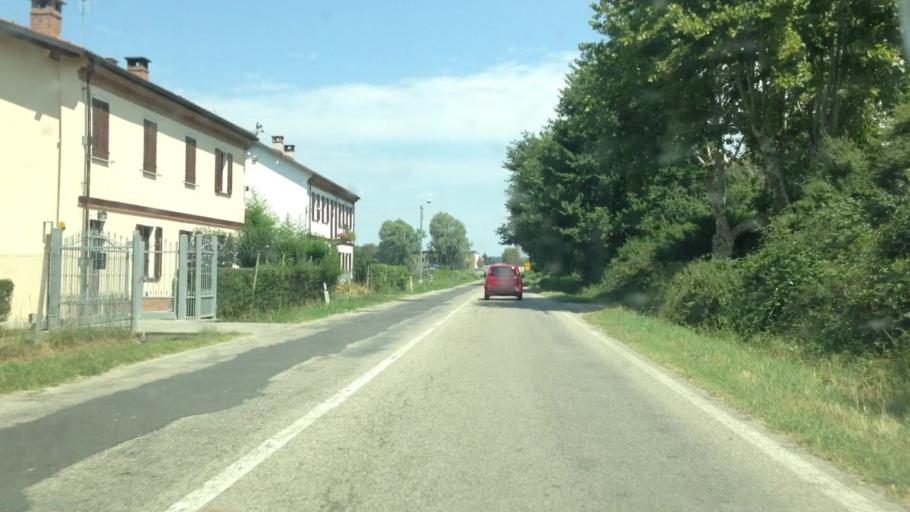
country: IT
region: Piedmont
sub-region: Provincia di Asti
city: Asti
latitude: 44.9316
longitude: 8.2253
